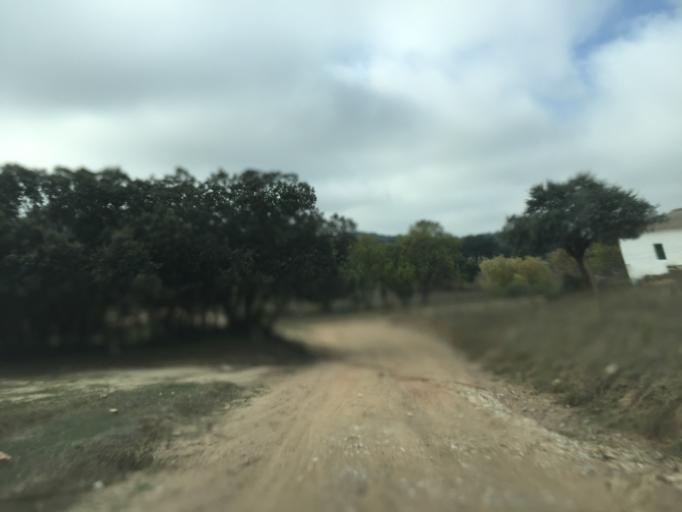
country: PT
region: Portalegre
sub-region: Fronteira
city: Fronteira
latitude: 39.0673
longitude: -7.6252
